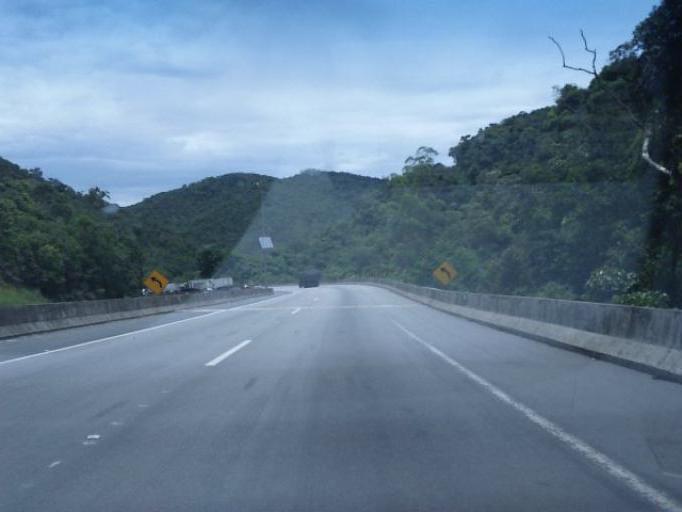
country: BR
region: Sao Paulo
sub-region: Juquitiba
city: Juquitiba
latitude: -24.0489
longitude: -47.1991
